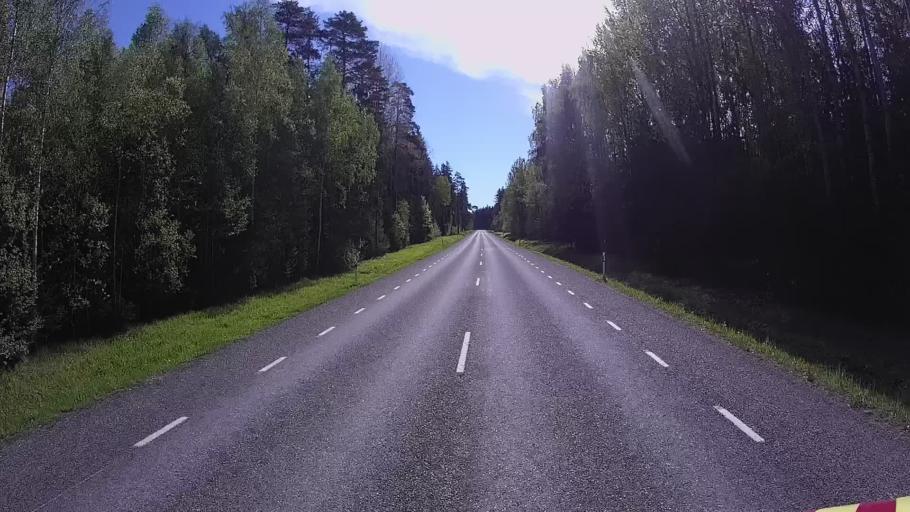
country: EE
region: Polvamaa
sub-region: Raepina vald
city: Rapina
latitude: 58.0985
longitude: 27.3906
